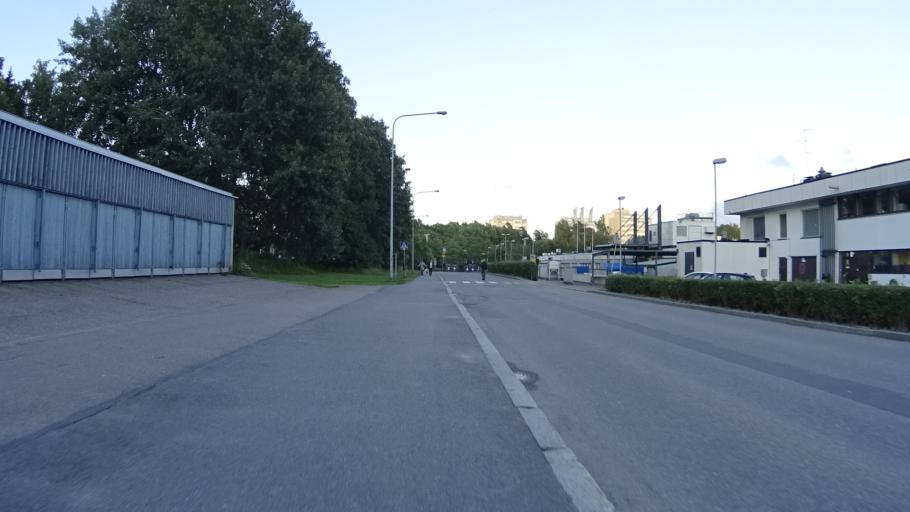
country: FI
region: Uusimaa
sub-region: Helsinki
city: Teekkarikylae
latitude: 60.2064
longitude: 24.8766
